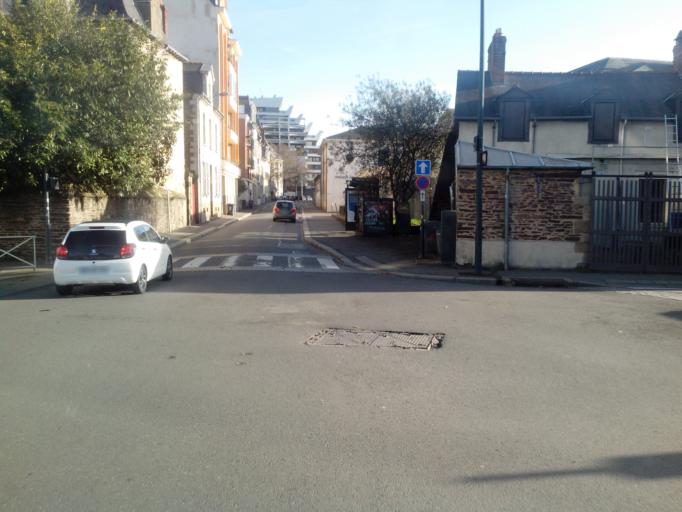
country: FR
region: Brittany
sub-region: Departement d'Ille-et-Vilaine
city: Rennes
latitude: 48.1172
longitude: -1.6778
